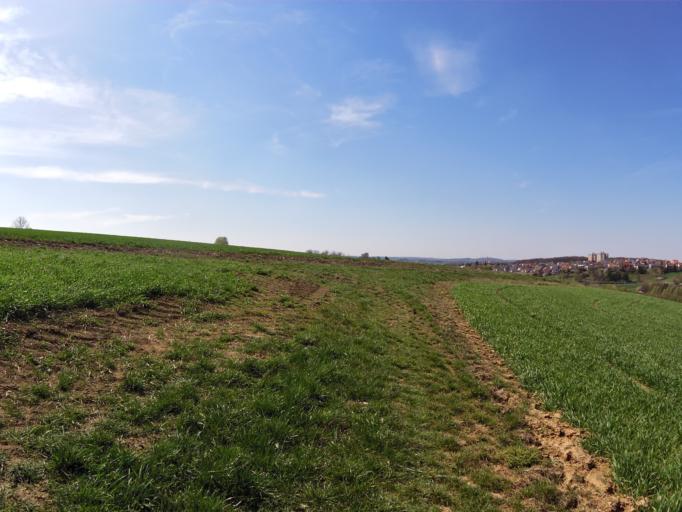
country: DE
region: Bavaria
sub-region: Regierungsbezirk Unterfranken
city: Rottendorf
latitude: 49.7983
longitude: 10.0390
